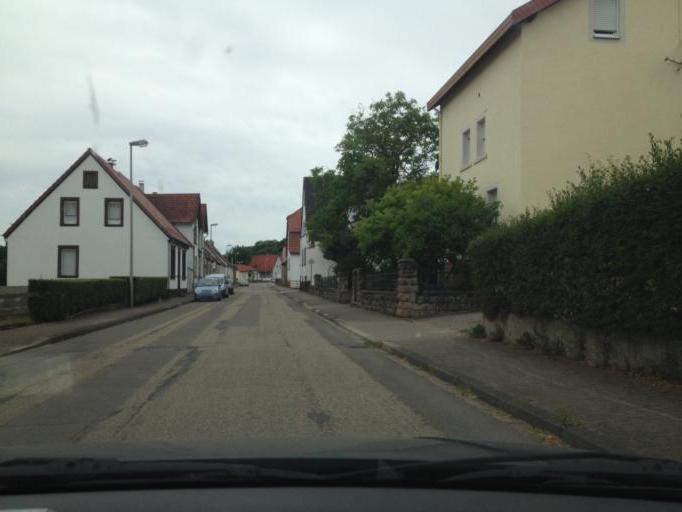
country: DE
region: Rheinland-Pfalz
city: Heltersberg
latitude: 49.3096
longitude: 7.7255
